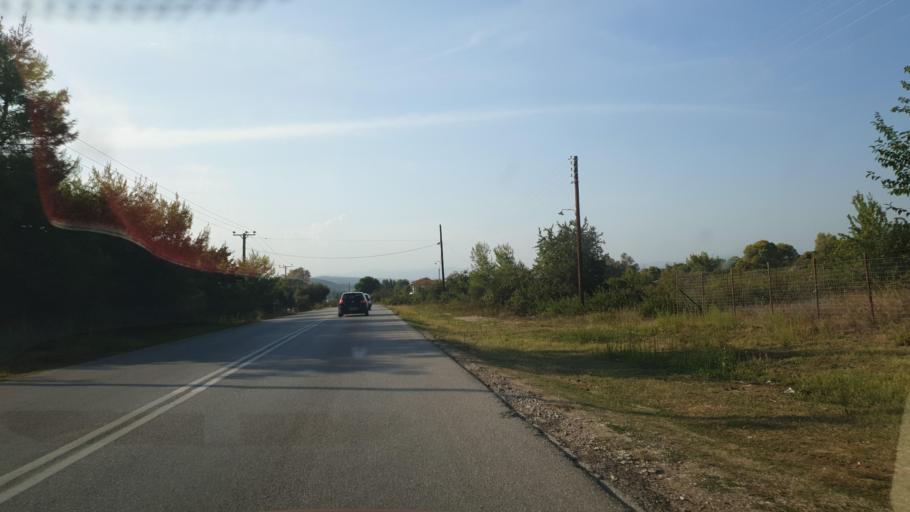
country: GR
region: Central Macedonia
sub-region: Nomos Chalkidikis
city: Agios Nikolaos
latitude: 40.2247
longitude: 23.7445
